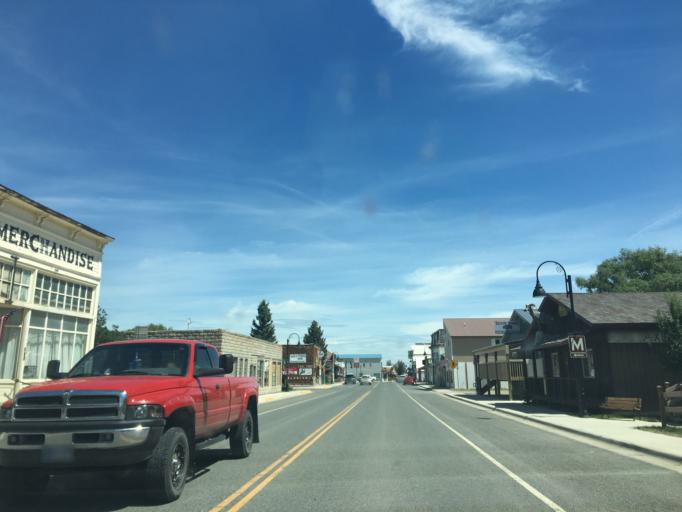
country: US
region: Montana
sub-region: Teton County
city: Choteau
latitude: 47.4921
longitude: -112.3925
